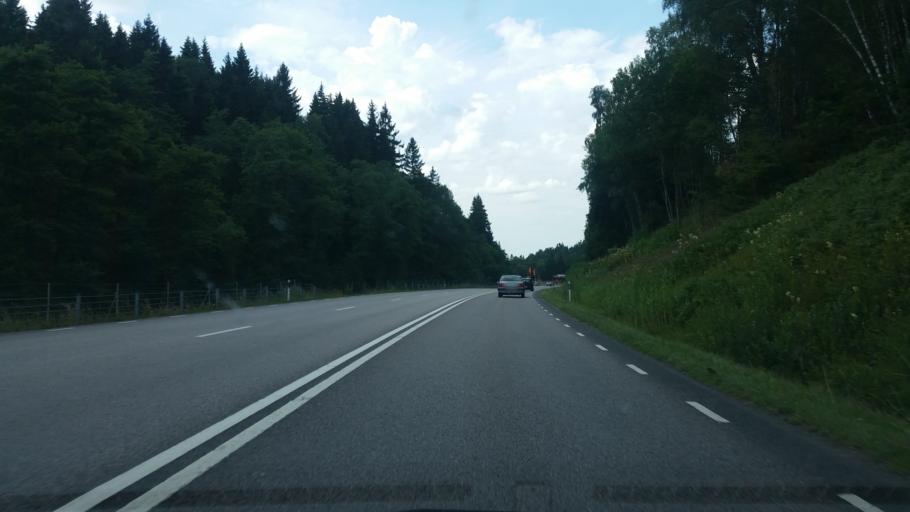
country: SE
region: Vaestra Goetaland
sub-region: Skovde Kommun
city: Skultorp
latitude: 58.3776
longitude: 13.7073
